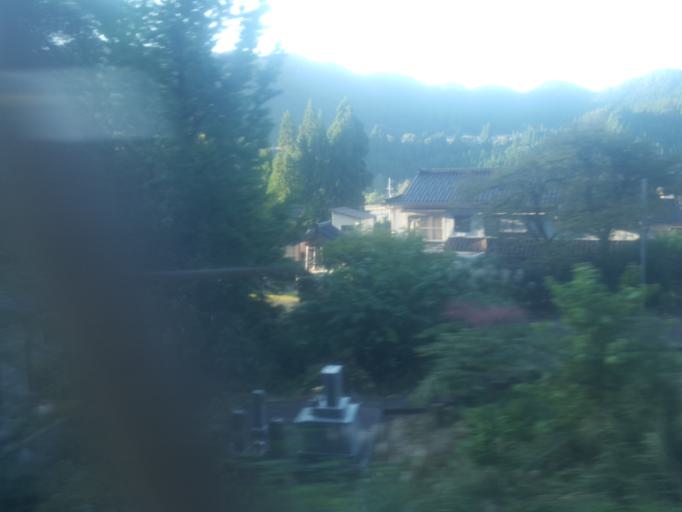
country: JP
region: Toyama
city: Kamiichi
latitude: 36.5737
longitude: 137.3942
